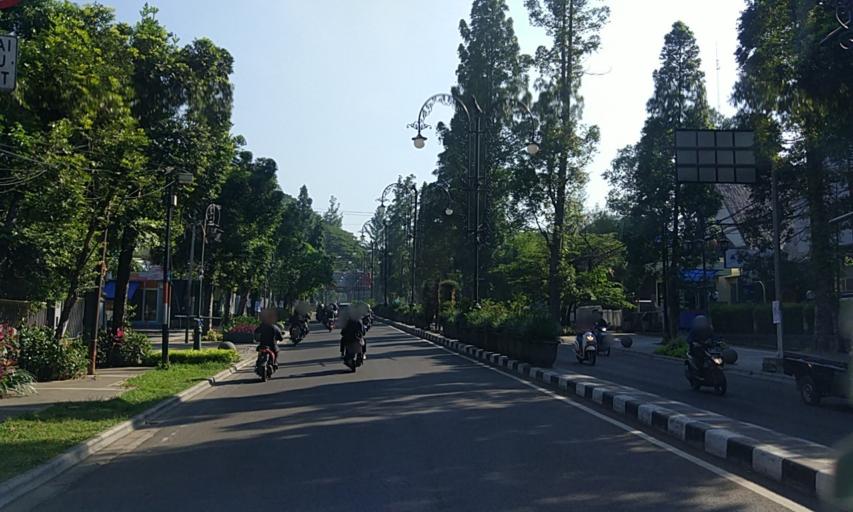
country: ID
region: West Java
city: Bandung
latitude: -6.8984
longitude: 107.6128
